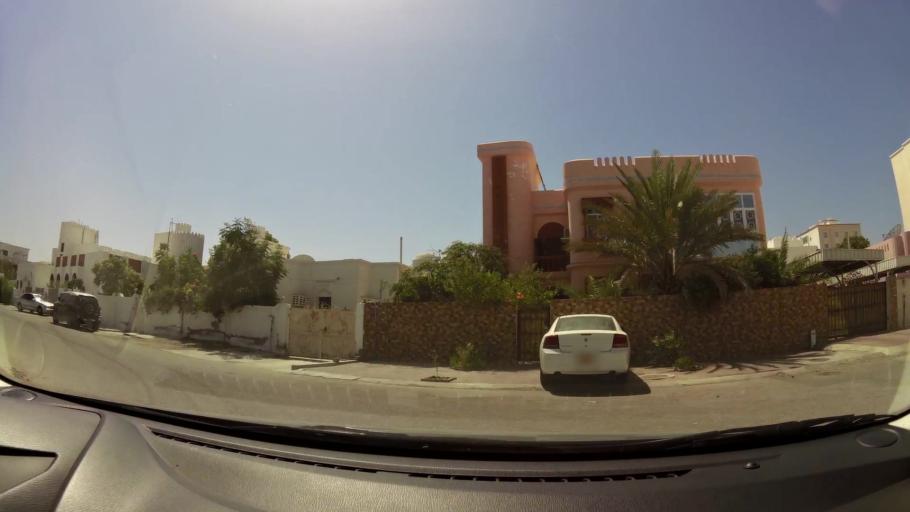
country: OM
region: Muhafazat Masqat
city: As Sib al Jadidah
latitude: 23.6250
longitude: 58.2183
